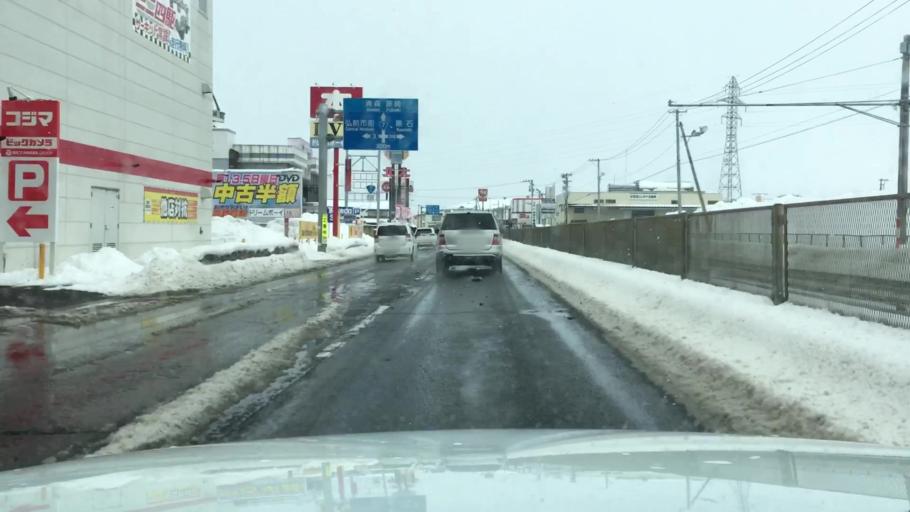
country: JP
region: Aomori
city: Hirosaki
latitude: 40.6078
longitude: 140.4989
